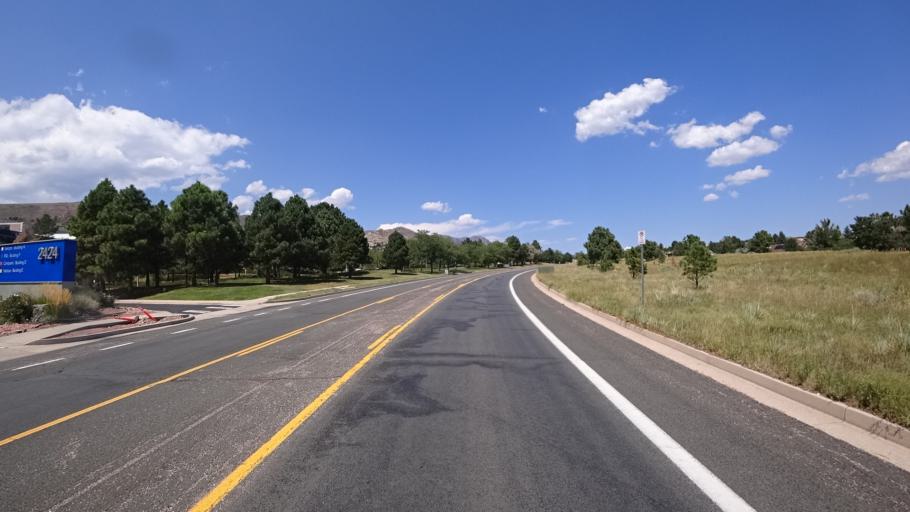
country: US
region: Colorado
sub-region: El Paso County
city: Manitou Springs
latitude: 38.9010
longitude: -104.8709
